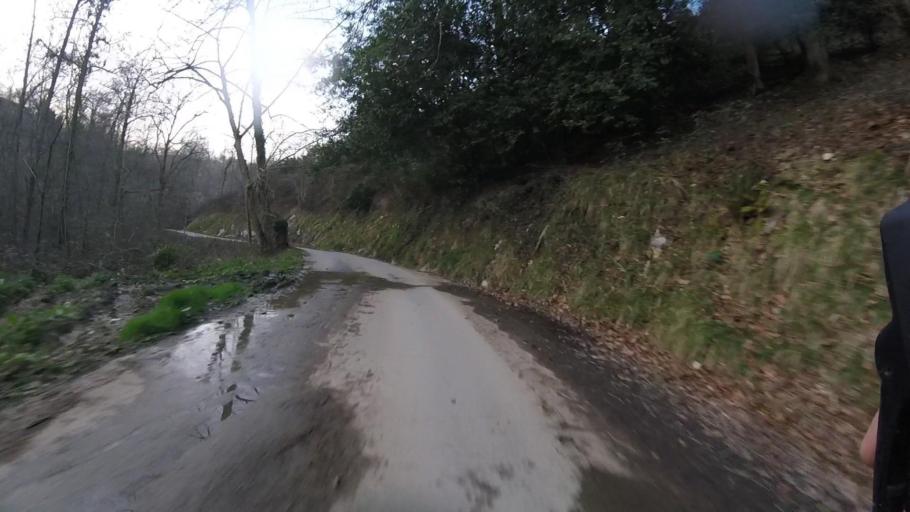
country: ES
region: Basque Country
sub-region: Provincia de Guipuzcoa
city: Errenteria
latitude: 43.2787
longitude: -1.8696
